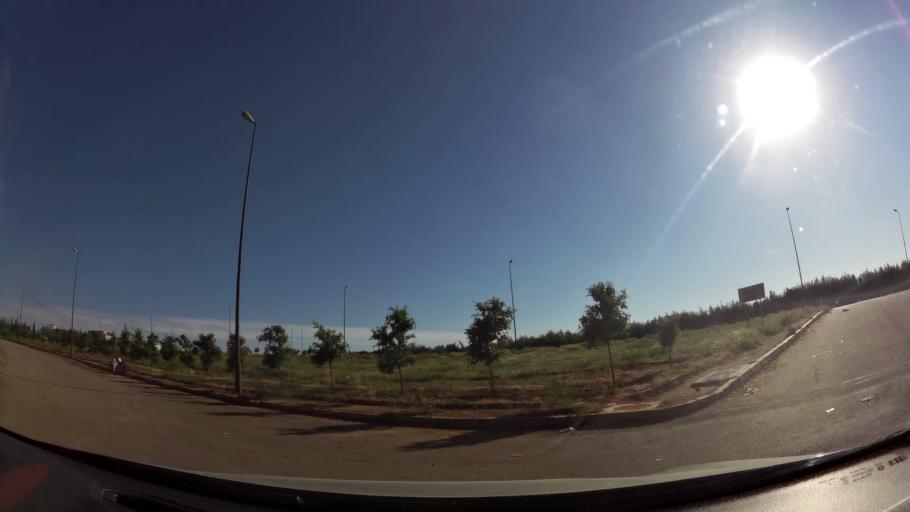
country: MA
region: Meknes-Tafilalet
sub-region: Meknes
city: Meknes
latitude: 33.8611
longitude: -5.5867
